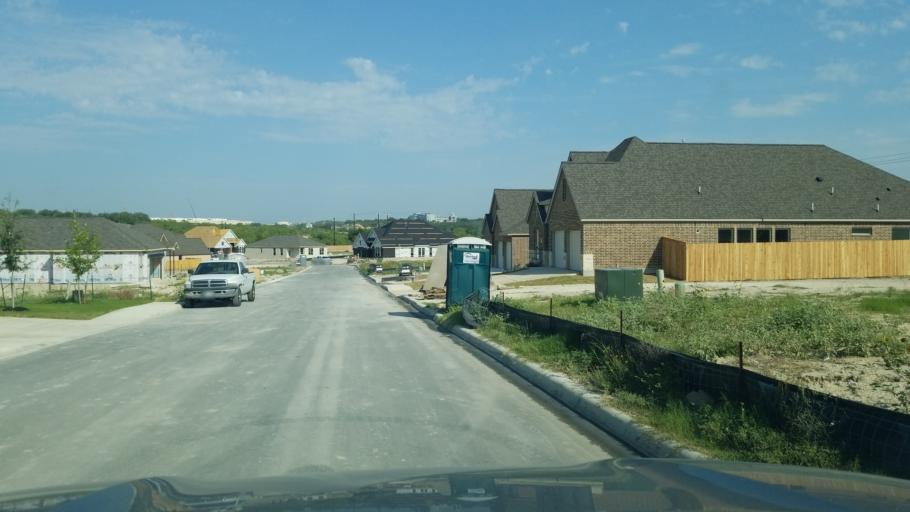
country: US
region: Texas
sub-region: Medina County
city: La Coste
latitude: 29.4074
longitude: -98.7859
